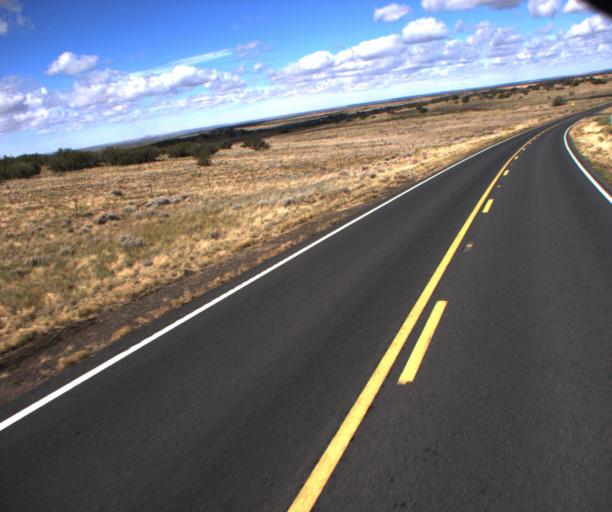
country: US
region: Arizona
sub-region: Apache County
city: Houck
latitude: 35.0834
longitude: -109.3072
